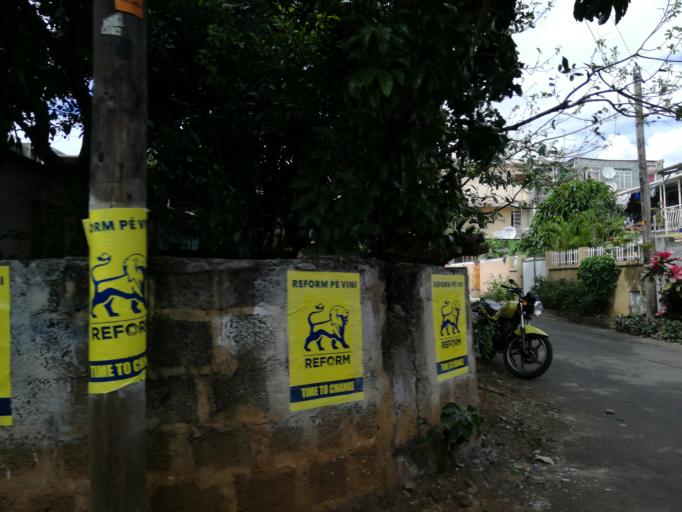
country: MU
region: Black River
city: Petite Riviere
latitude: -20.2159
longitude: 57.4651
